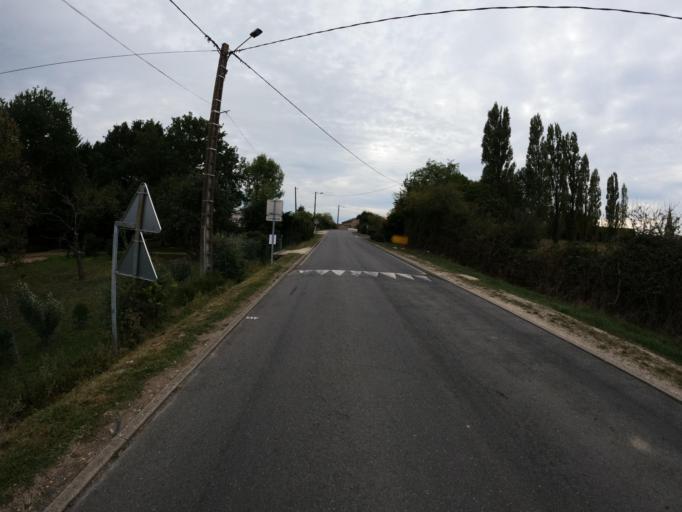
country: FR
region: Poitou-Charentes
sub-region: Departement de la Vienne
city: Saulge
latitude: 46.3305
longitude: 0.8162
